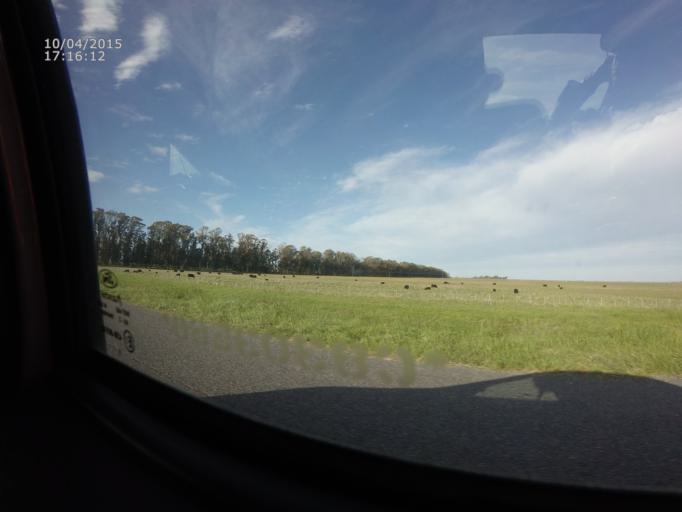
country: AR
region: Buenos Aires
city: Coronel Vidal
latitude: -37.2185
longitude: -57.7941
